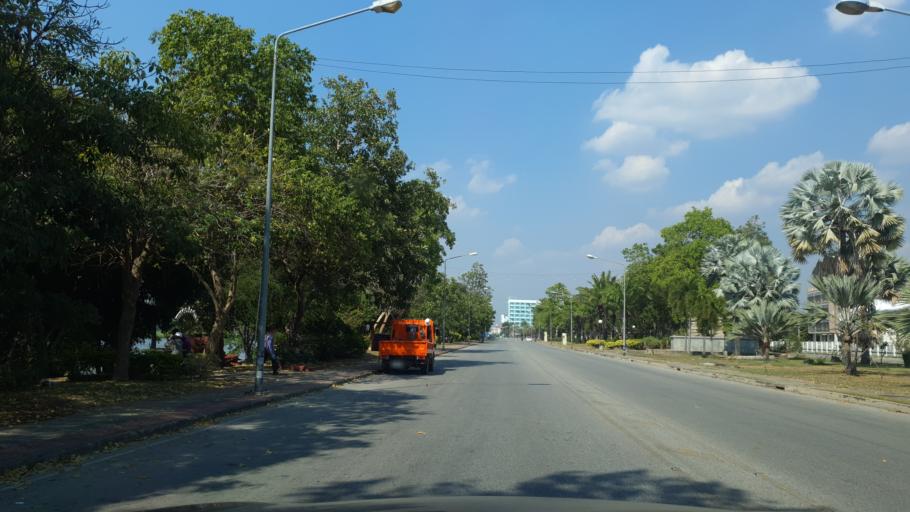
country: TH
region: Tak
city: Tak
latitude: 16.8668
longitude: 99.1241
